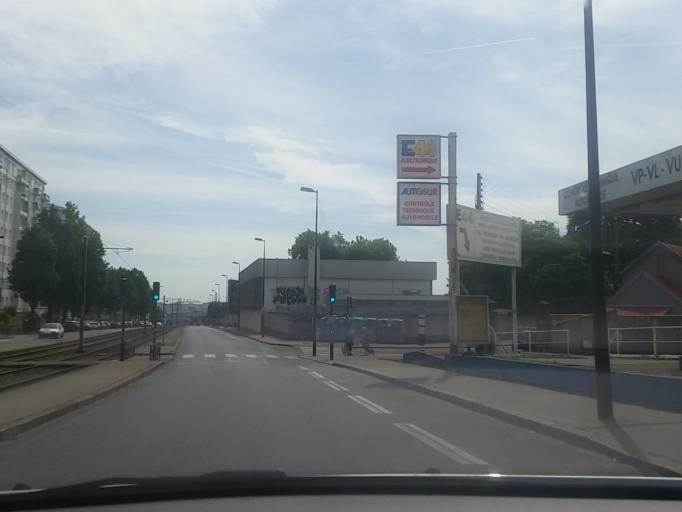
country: FR
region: Pays de la Loire
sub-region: Departement de la Loire-Atlantique
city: Nantes
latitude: 47.2086
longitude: -1.5866
